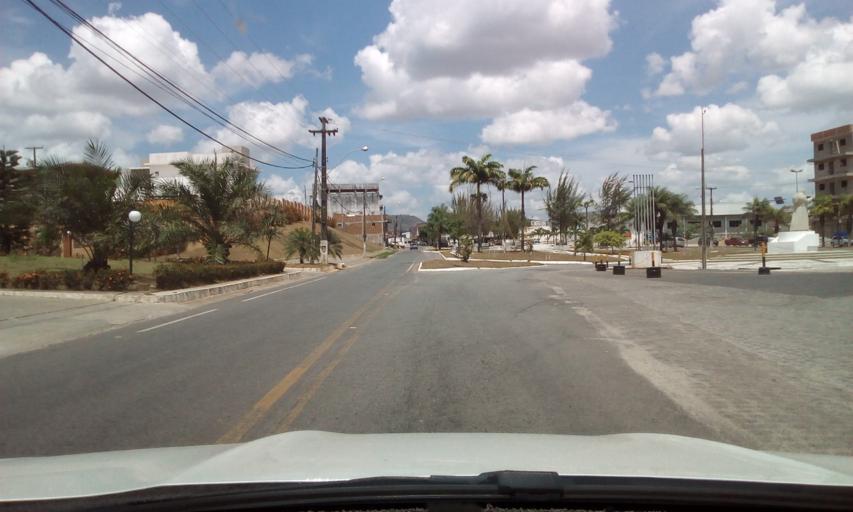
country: BR
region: Paraiba
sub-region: Guarabira
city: Guarabira
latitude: -6.8587
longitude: -35.4969
